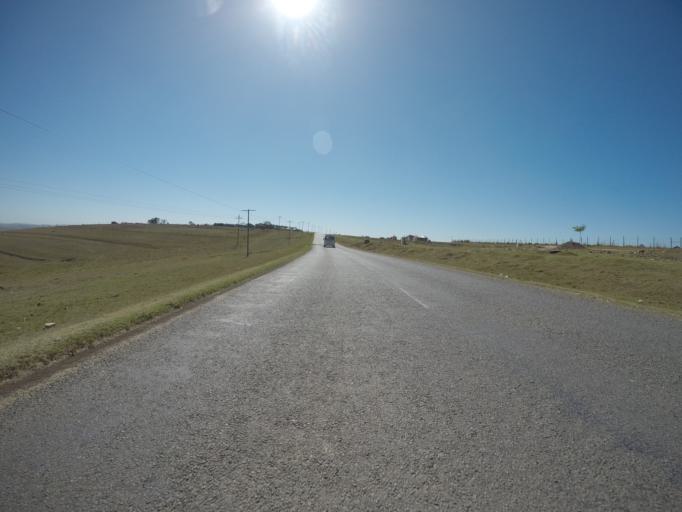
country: ZA
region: Eastern Cape
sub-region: OR Tambo District Municipality
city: Mthatha
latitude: -31.8927
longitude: 28.7710
